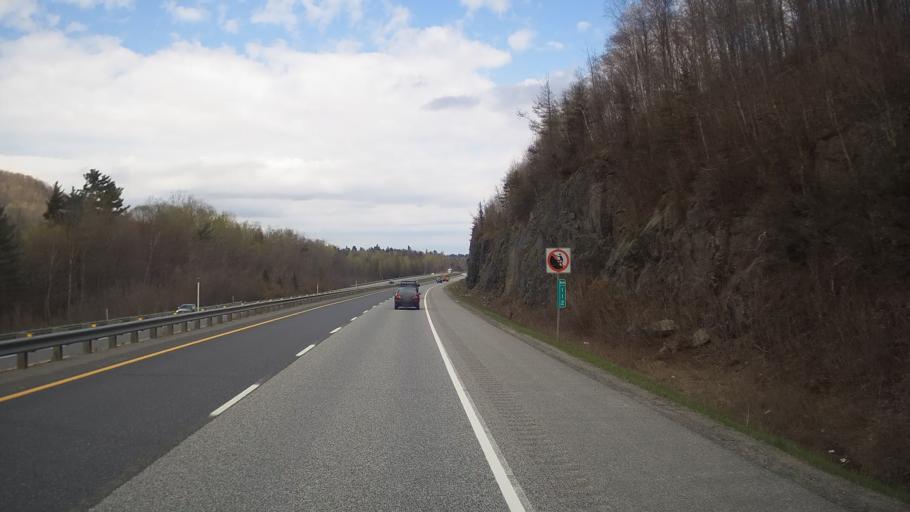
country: CA
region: Quebec
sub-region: Estrie
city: Magog
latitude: 45.2909
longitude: -72.2393
